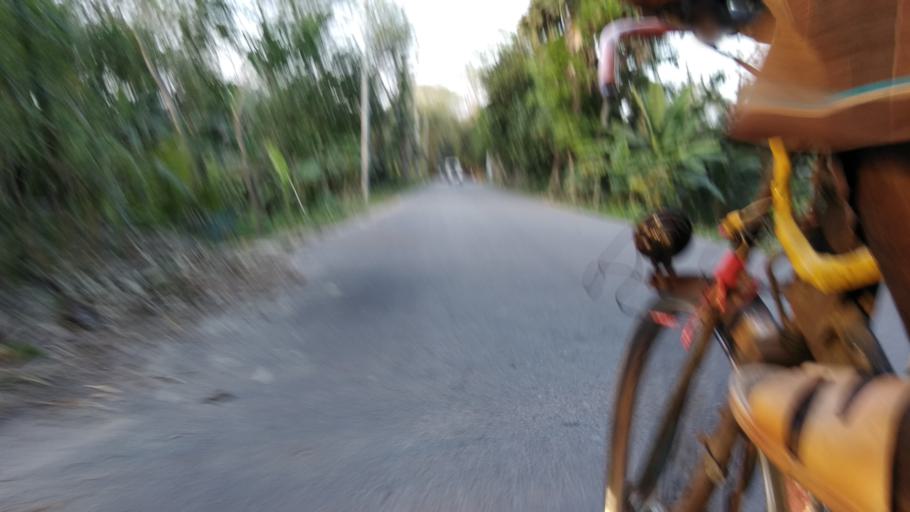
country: BD
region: Barisal
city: Mehendiganj
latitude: 22.9336
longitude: 90.4059
